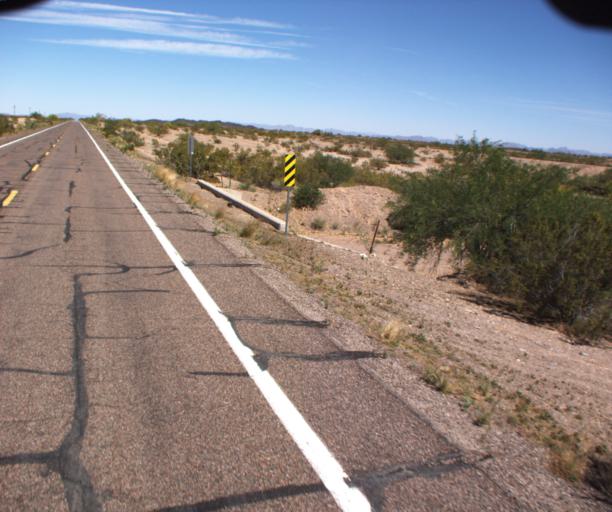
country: US
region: Arizona
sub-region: Maricopa County
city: Gila Bend
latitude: 32.7813
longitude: -112.8100
